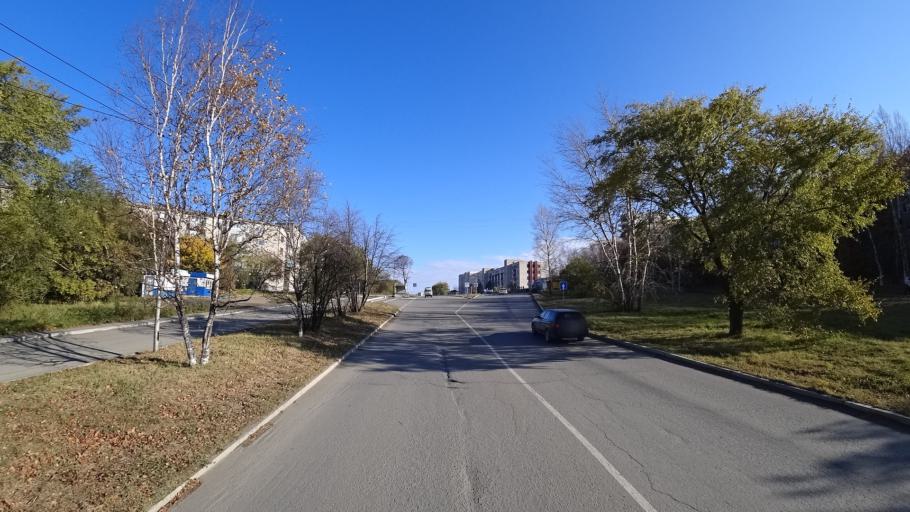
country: RU
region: Khabarovsk Krai
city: Amursk
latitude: 50.2411
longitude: 136.9129
